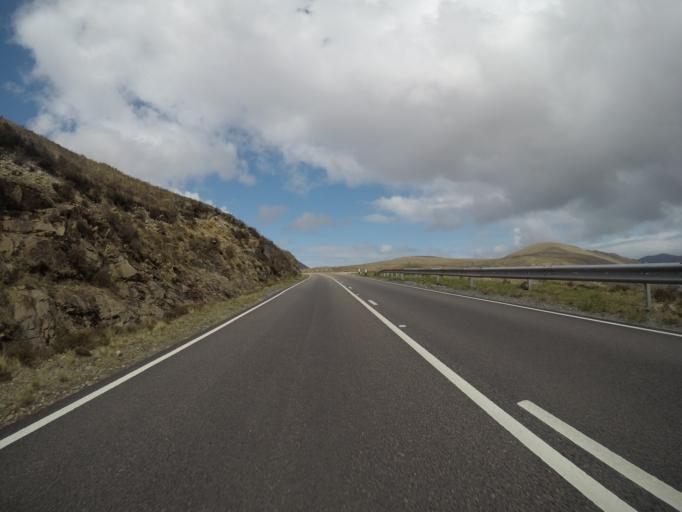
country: GB
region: Scotland
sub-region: Highland
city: Portree
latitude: 57.2716
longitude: -6.0897
